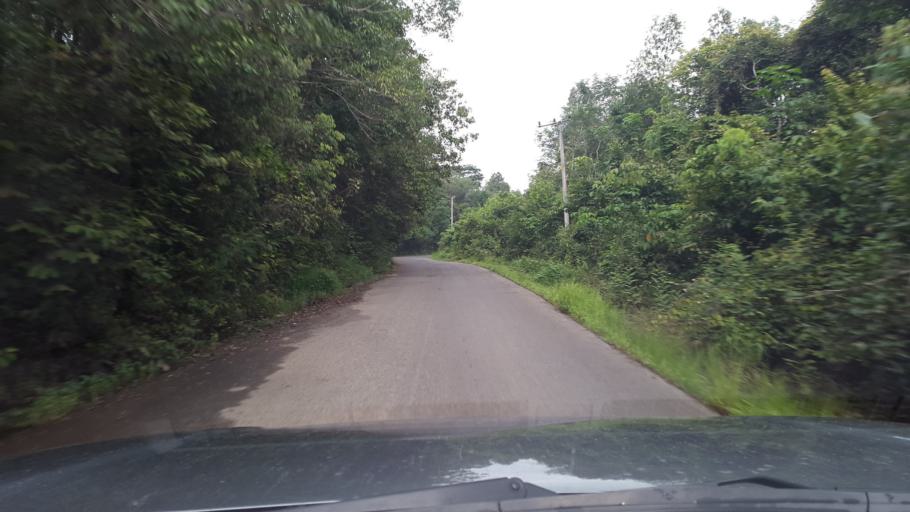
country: ID
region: South Sumatra
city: Gunungmenang
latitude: -3.1673
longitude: 103.9501
